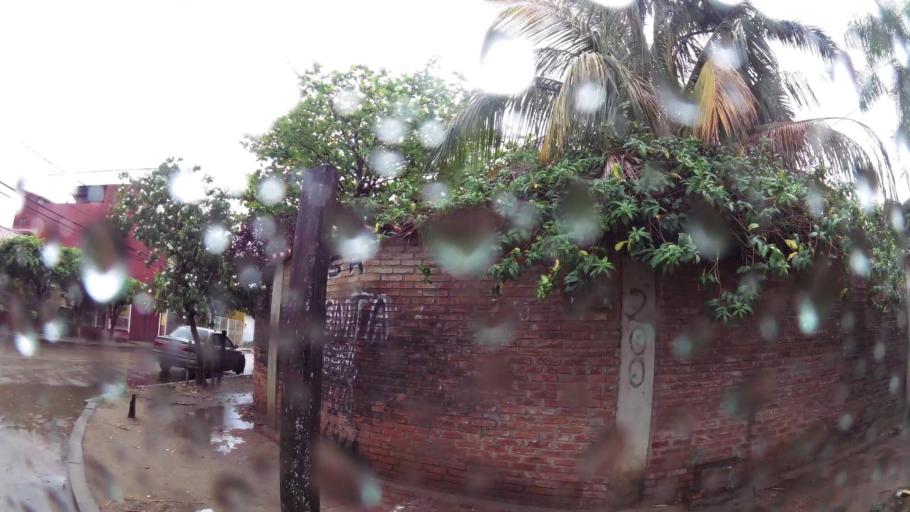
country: BO
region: Santa Cruz
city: Santa Cruz de la Sierra
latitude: -17.7948
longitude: -63.2079
